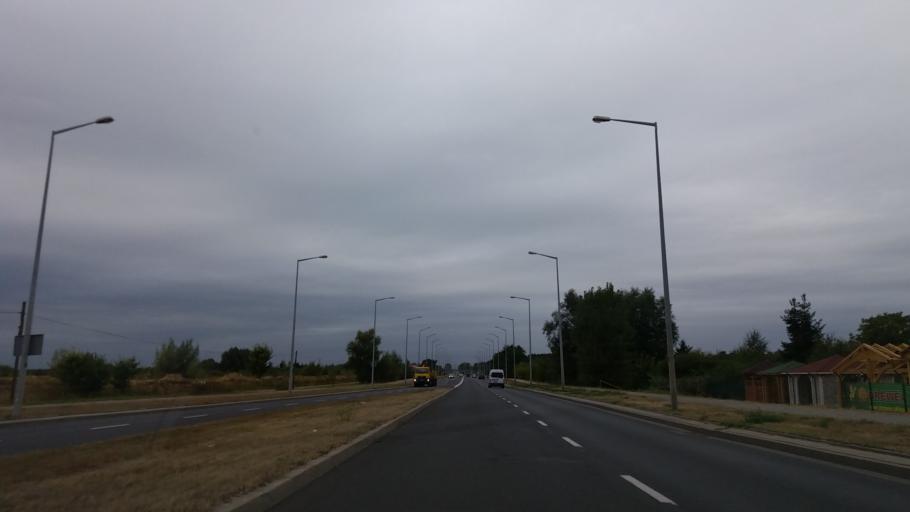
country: PL
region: Lubusz
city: Gorzow Wielkopolski
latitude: 52.7087
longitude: 15.2402
